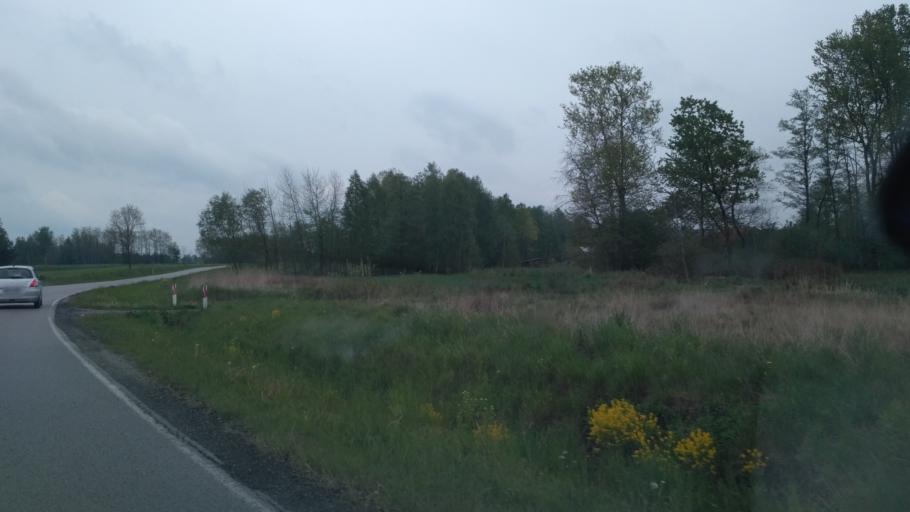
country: PL
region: Subcarpathian Voivodeship
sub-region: Powiat ropczycko-sedziszowski
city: Sedziszow Malopolski
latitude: 50.0948
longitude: 21.7300
